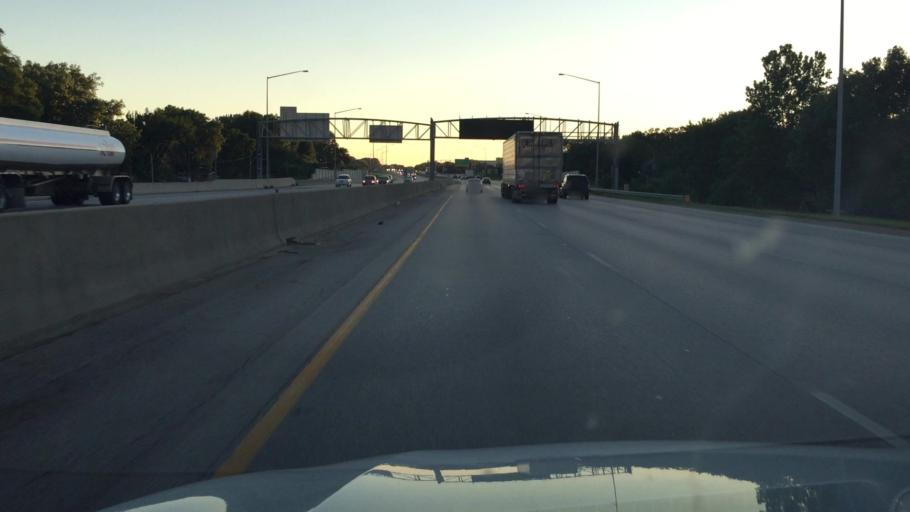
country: US
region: Iowa
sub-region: Polk County
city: Clive
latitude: 41.5934
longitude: -93.7256
